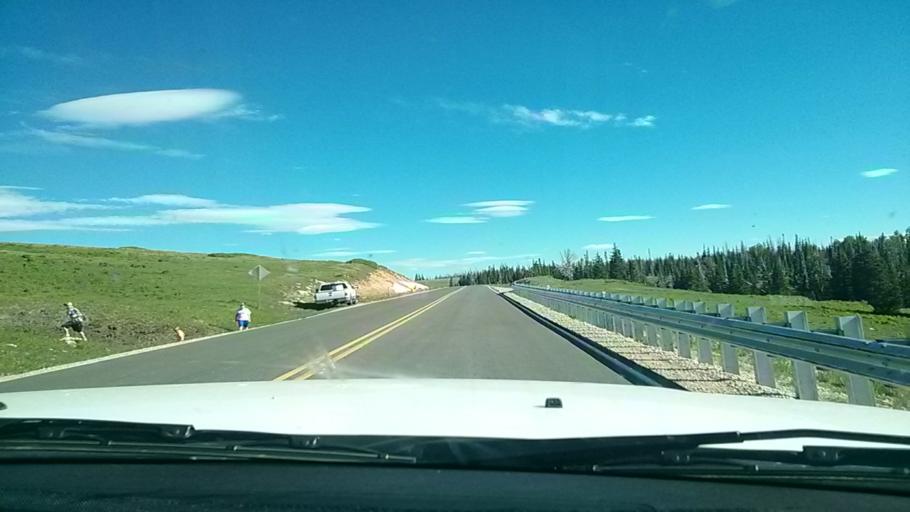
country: US
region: Utah
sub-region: Iron County
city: Parowan
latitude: 37.6748
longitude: -112.8417
